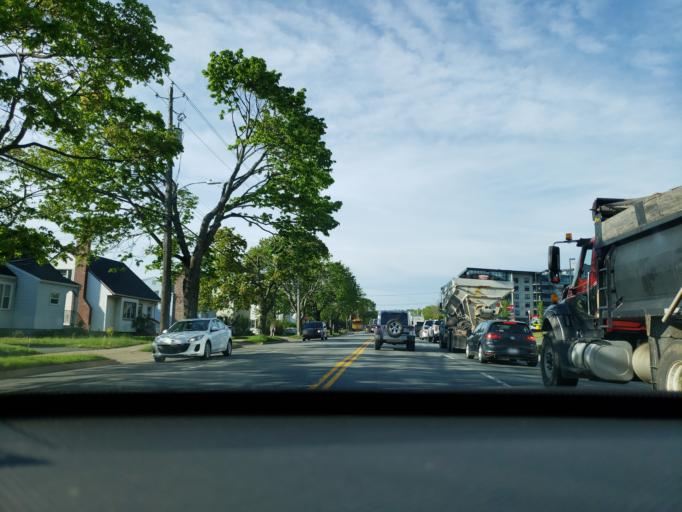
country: CA
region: Nova Scotia
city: Dartmouth
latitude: 44.6553
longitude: -63.6299
